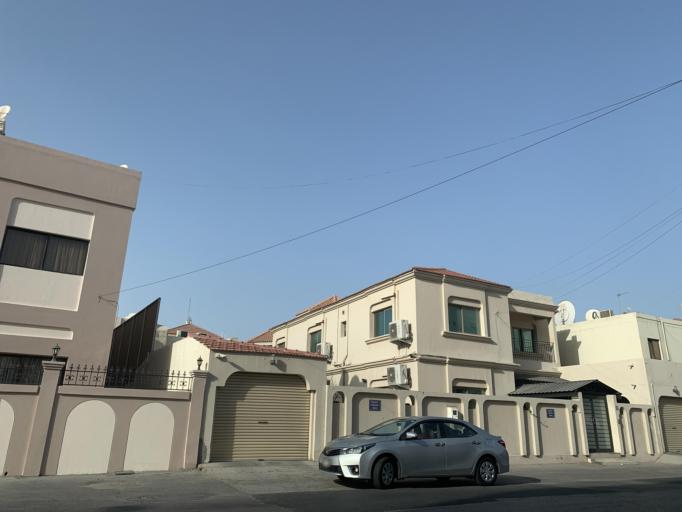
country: BH
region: Manama
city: Manama
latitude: 26.2059
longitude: 50.5816
